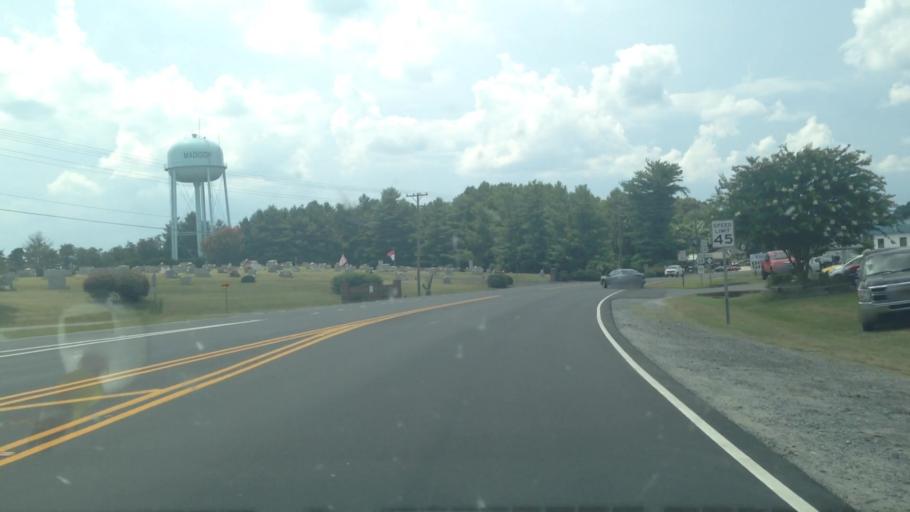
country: US
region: North Carolina
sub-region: Rockingham County
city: Madison
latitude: 36.3755
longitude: -79.9437
